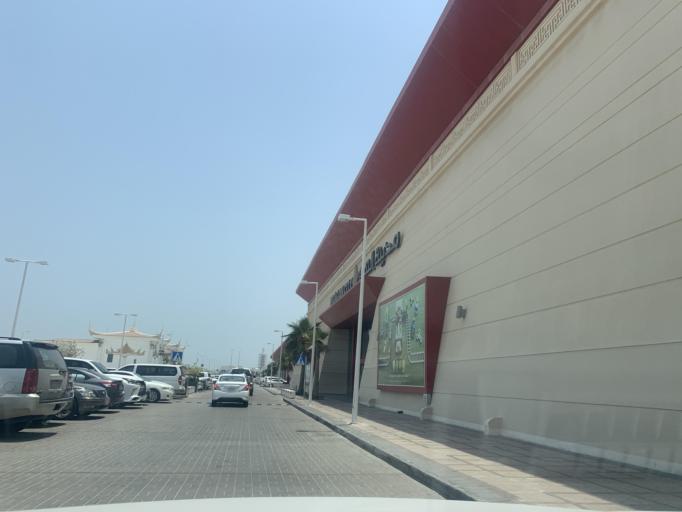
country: BH
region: Muharraq
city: Al Muharraq
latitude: 26.3064
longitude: 50.6248
